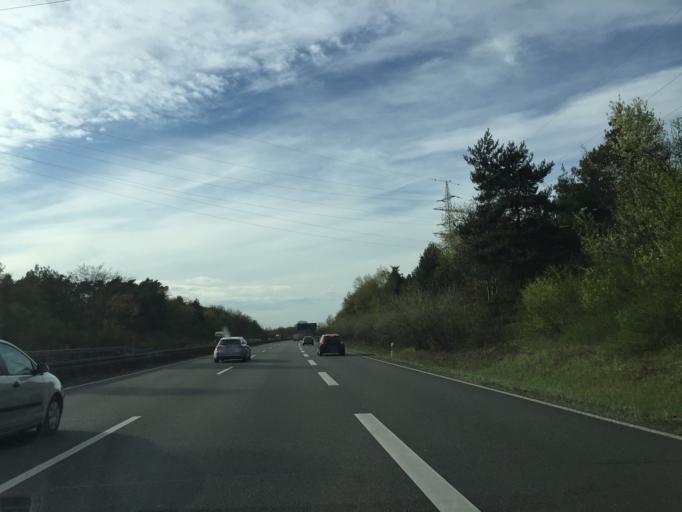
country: DE
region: Hesse
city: Griesheim
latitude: 49.8500
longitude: 8.6090
